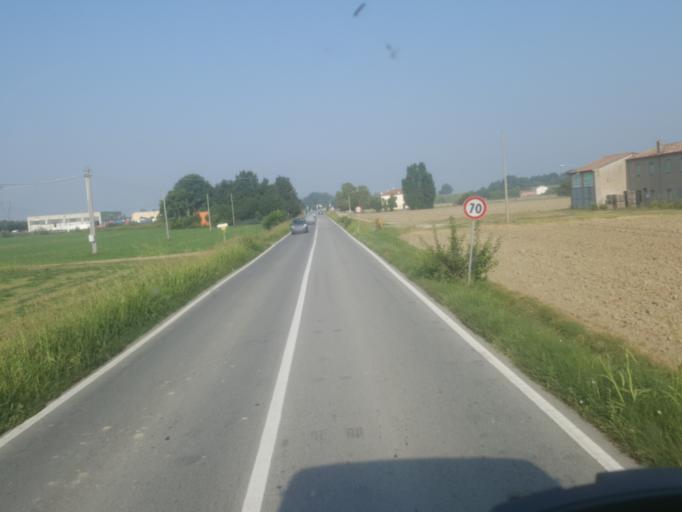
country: IT
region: Emilia-Romagna
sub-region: Provincia di Ravenna
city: Voltana
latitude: 44.5519
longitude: 11.9478
